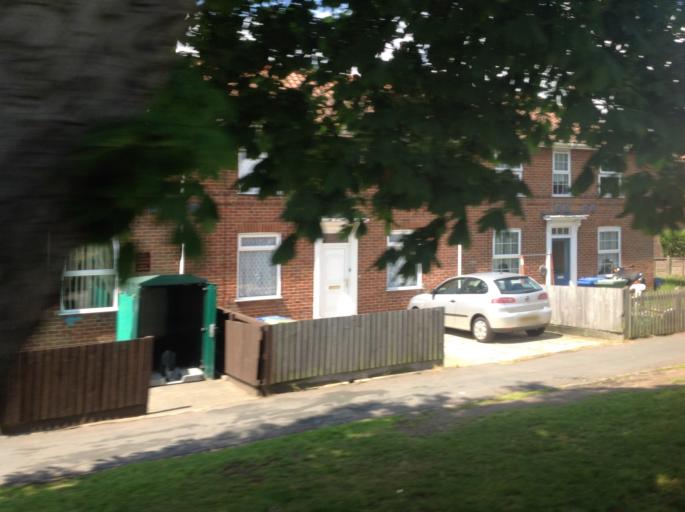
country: GB
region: England
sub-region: Norfolk
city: Norwich
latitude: 52.6523
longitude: 1.2796
